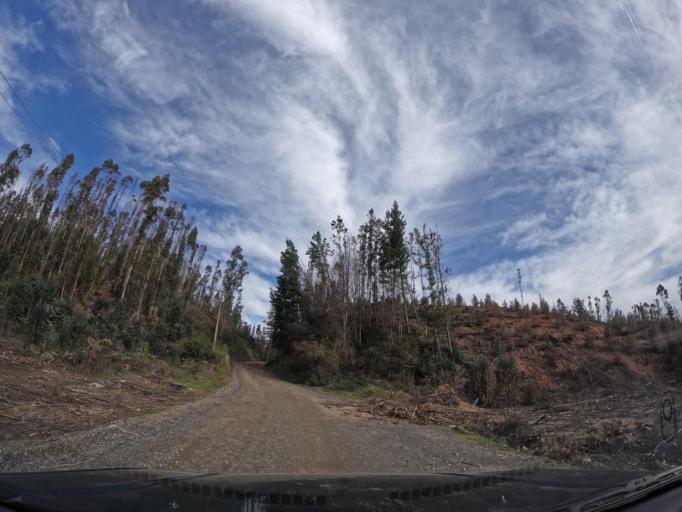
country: CL
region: Biobio
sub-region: Provincia de Concepcion
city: Chiguayante
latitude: -37.0101
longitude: -72.9107
